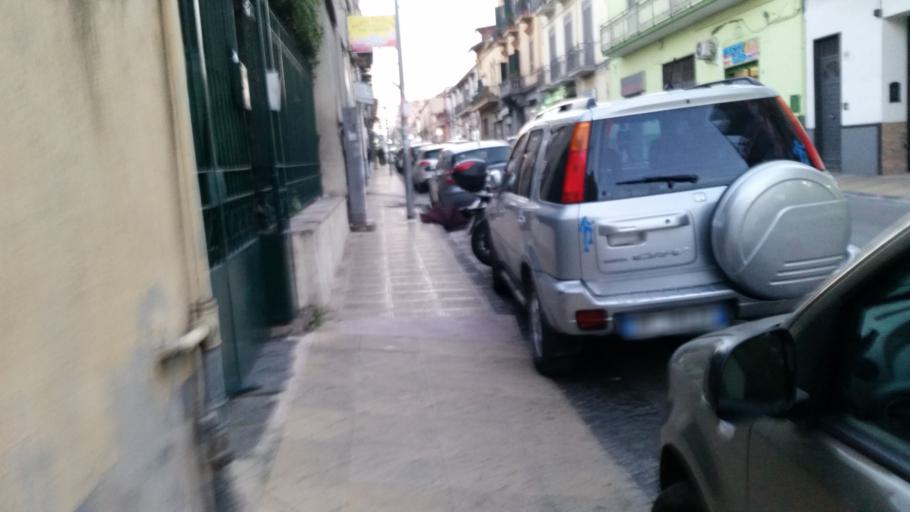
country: IT
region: Campania
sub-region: Provincia di Napoli
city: Mugnano di Napoli
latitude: 40.9060
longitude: 14.2074
